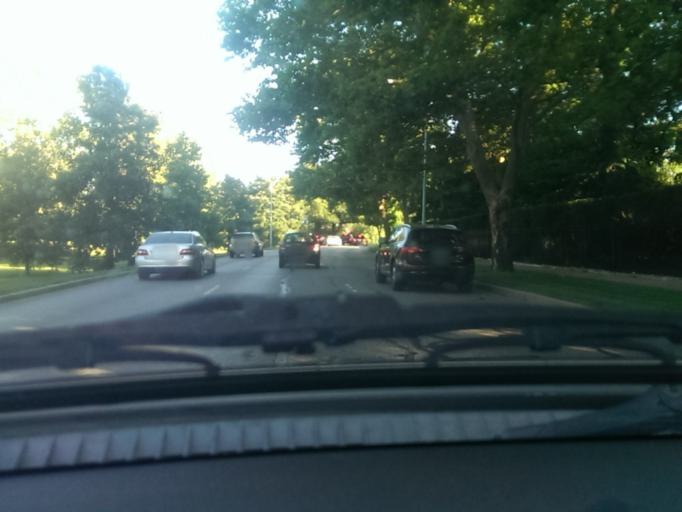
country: US
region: Kansas
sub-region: Johnson County
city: Westwood
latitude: 39.0295
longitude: -94.6044
